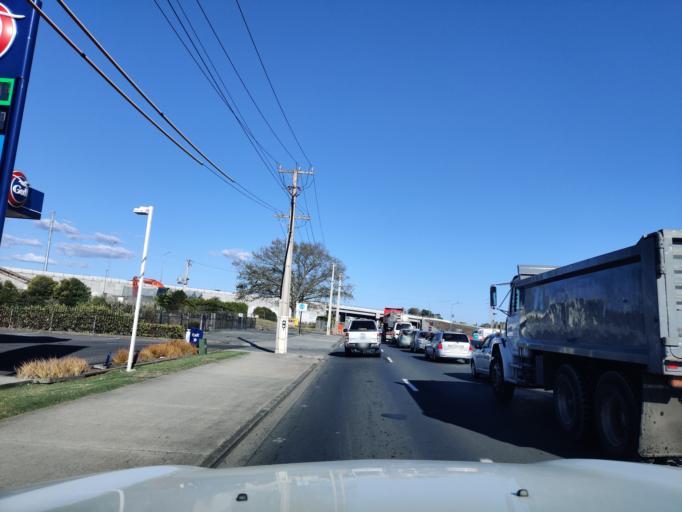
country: NZ
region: Auckland
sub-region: Auckland
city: Takanini
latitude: -37.0347
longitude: 174.9080
